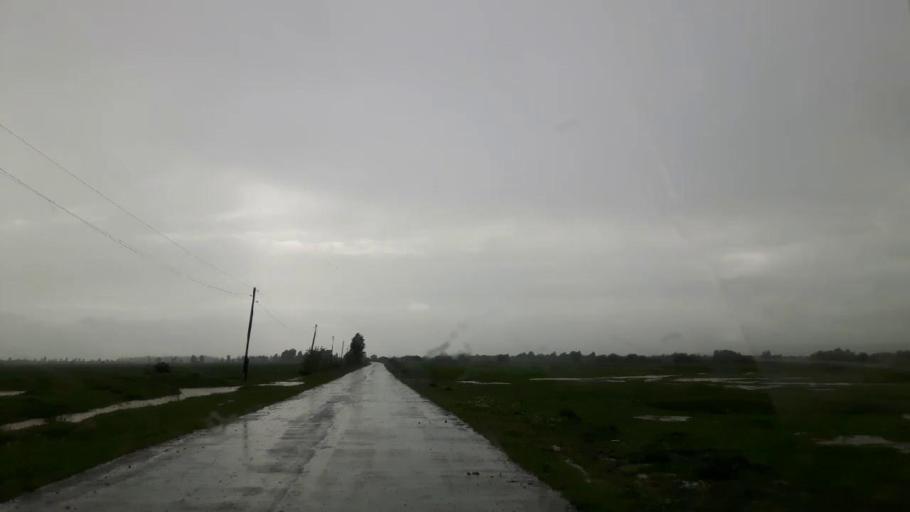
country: GE
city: Agara
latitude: 42.0147
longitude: 43.8140
